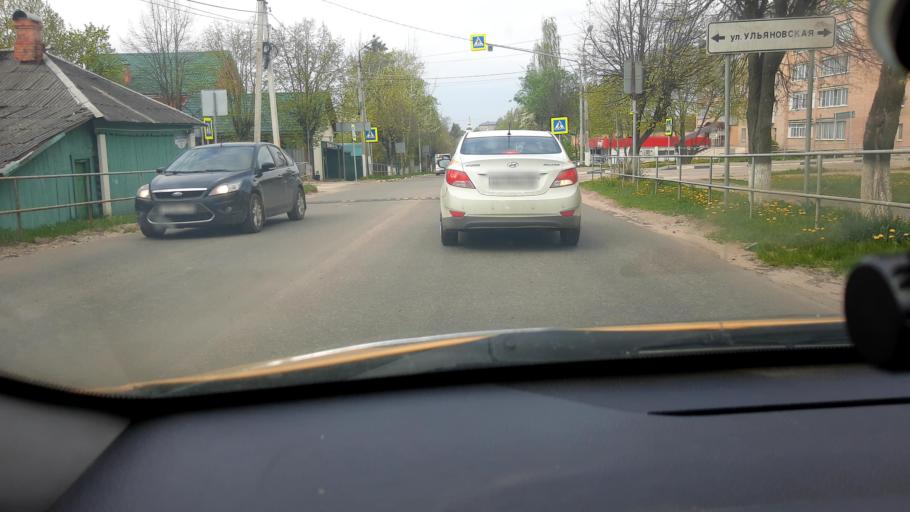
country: RU
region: Moskovskaya
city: Ruza
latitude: 55.7024
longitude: 36.2008
